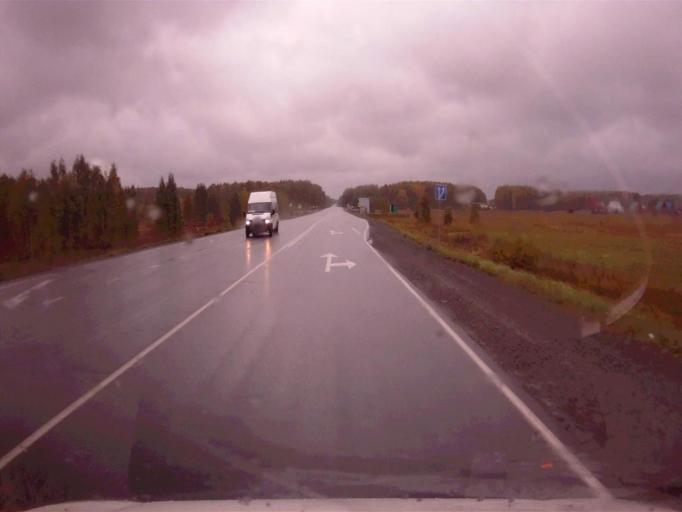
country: RU
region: Chelyabinsk
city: Argayash
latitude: 55.4555
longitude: 60.9287
